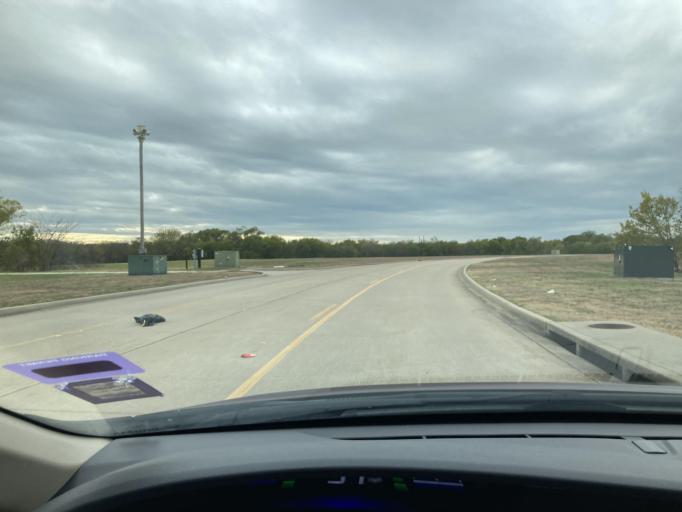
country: US
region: Texas
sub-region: Navarro County
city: Corsicana
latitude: 32.0639
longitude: -96.4439
